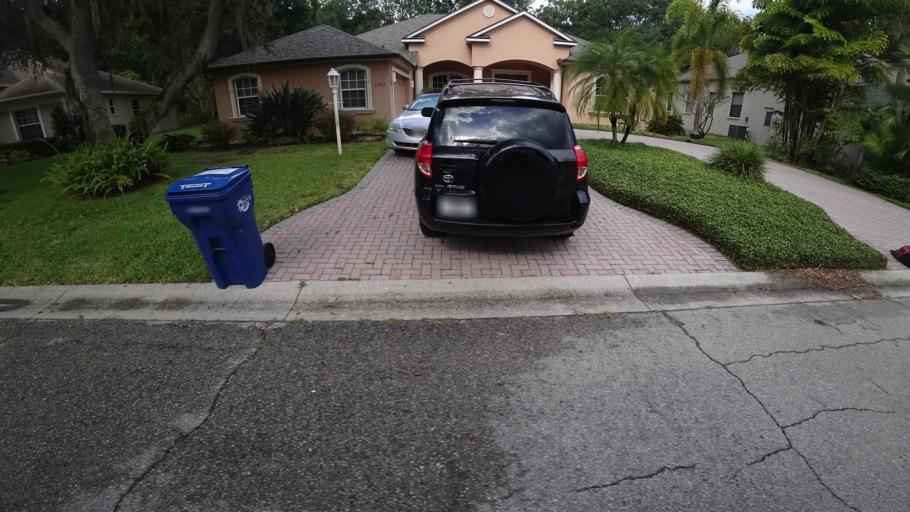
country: US
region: Florida
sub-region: Sarasota County
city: The Meadows
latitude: 27.4165
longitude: -82.4318
